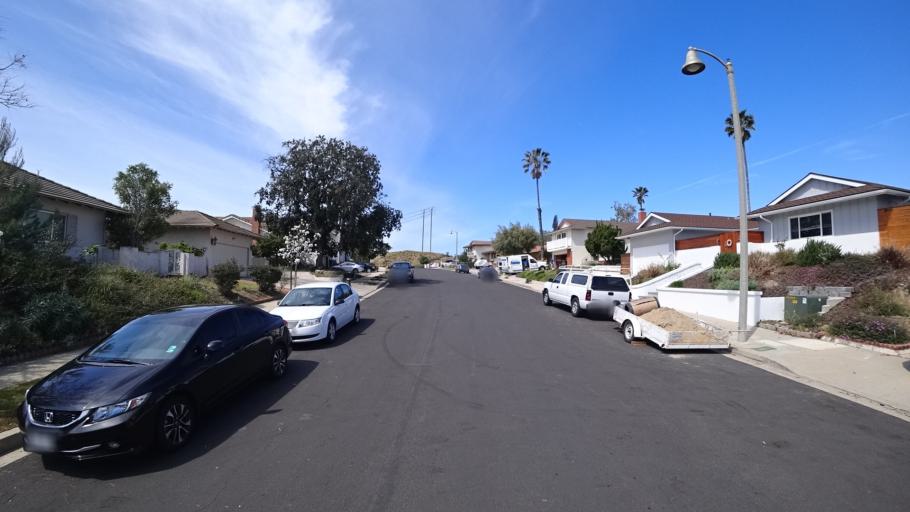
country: US
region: California
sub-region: Ventura County
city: Moorpark
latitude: 34.2327
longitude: -118.8646
